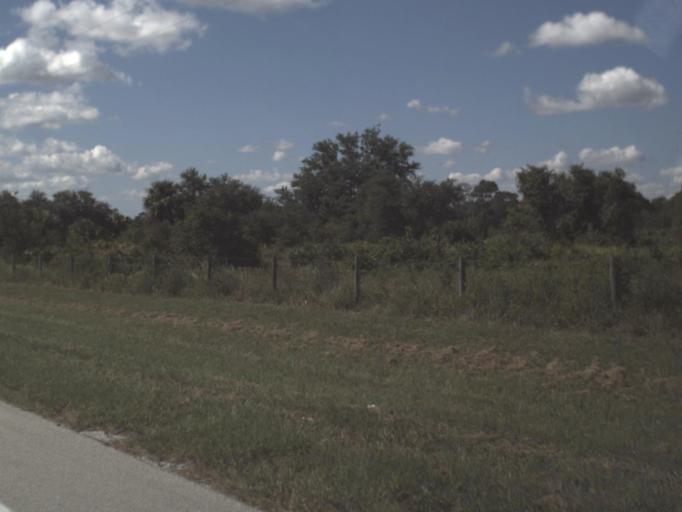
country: US
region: Florida
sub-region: Hendry County
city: Port LaBelle
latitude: 26.8128
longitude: -81.3506
